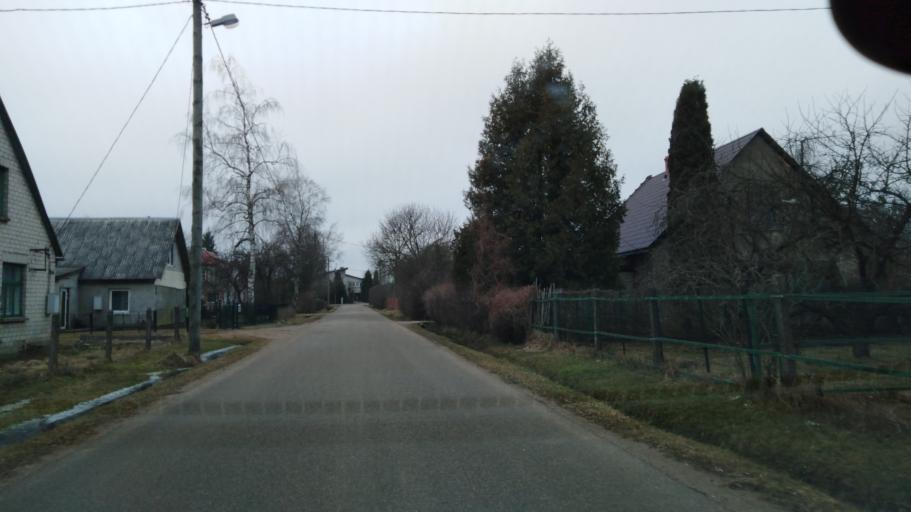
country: LV
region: Kuldigas Rajons
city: Kuldiga
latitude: 56.9757
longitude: 21.9809
